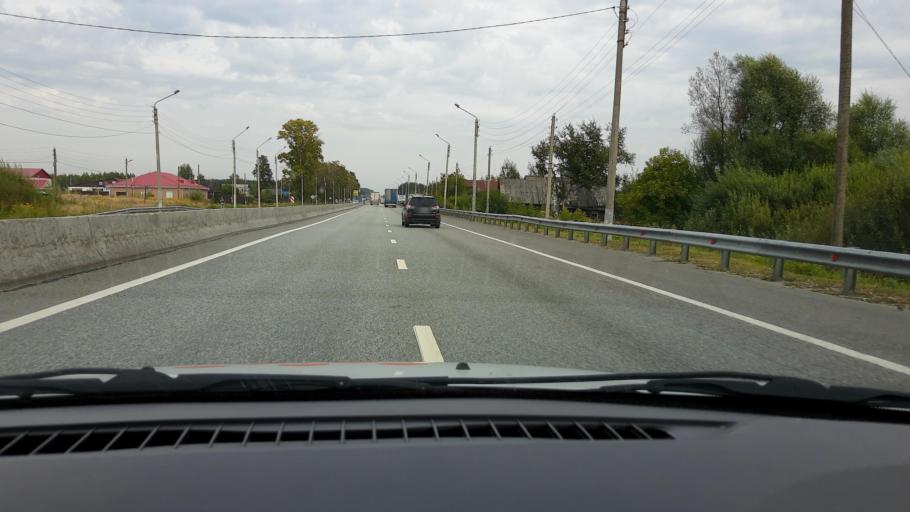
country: RU
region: Nizjnij Novgorod
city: Novosmolinskiy
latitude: 56.2773
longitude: 42.9863
